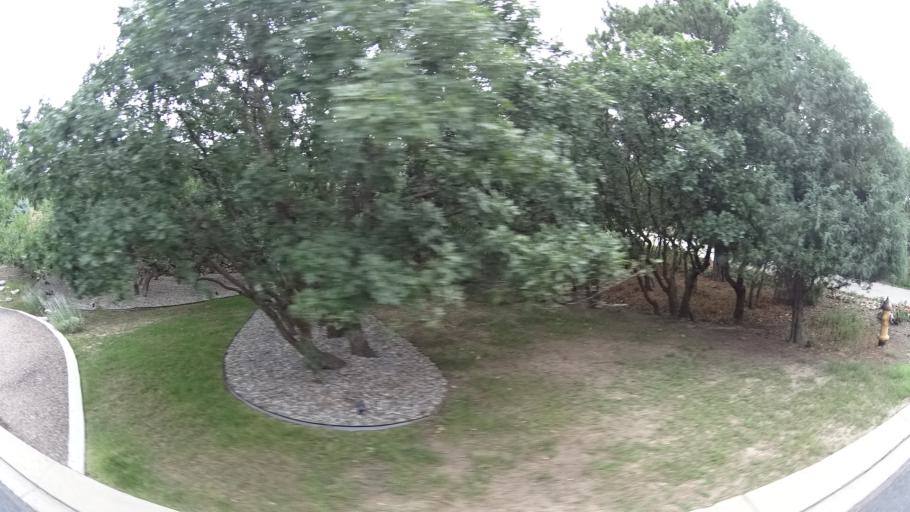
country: US
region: Colorado
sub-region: El Paso County
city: Air Force Academy
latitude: 38.9307
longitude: -104.8502
